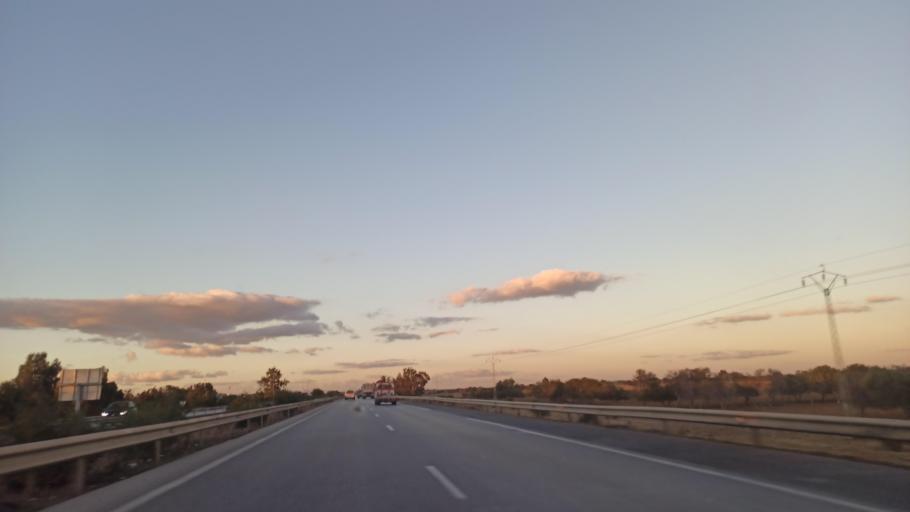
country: TN
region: Susah
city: Harqalah
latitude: 36.1271
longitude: 10.4064
